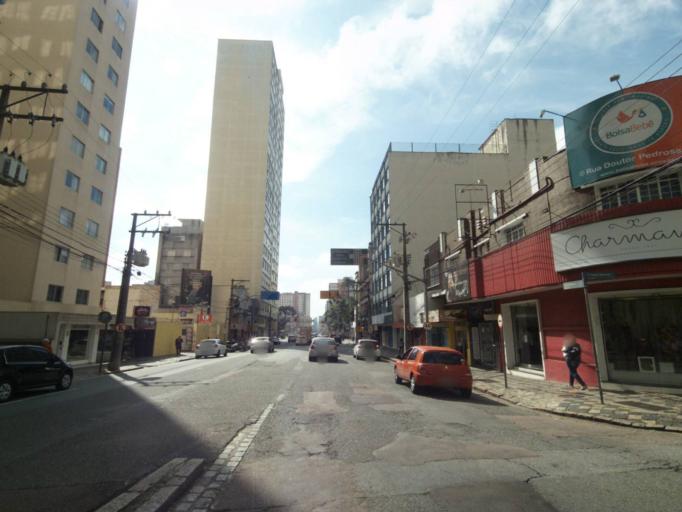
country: BR
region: Parana
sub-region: Curitiba
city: Curitiba
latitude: -25.4375
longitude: -49.2755
